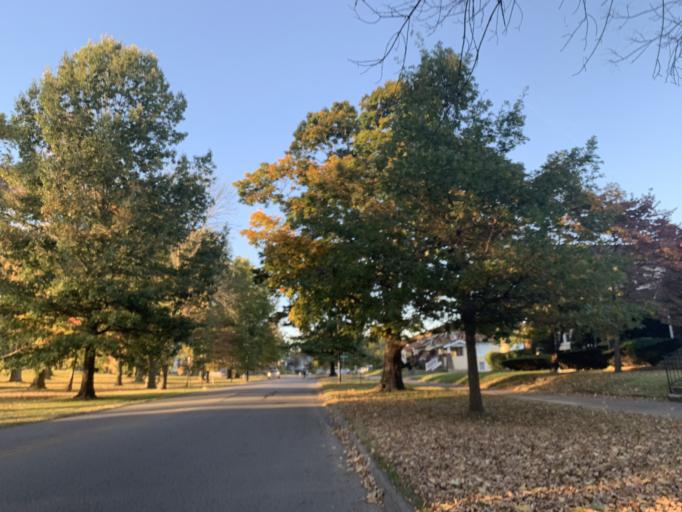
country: US
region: Indiana
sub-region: Floyd County
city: New Albany
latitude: 38.2590
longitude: -85.8240
